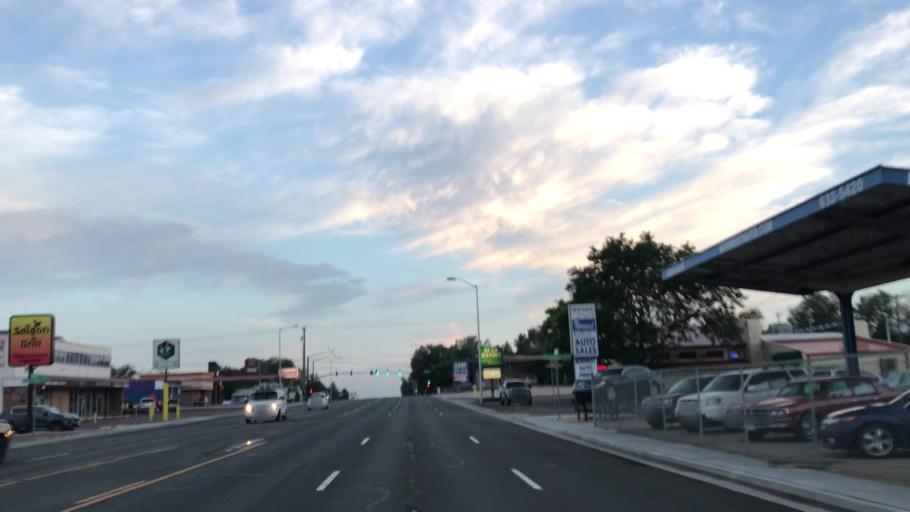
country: US
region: Colorado
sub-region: El Paso County
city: Colorado Springs
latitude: 38.8375
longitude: -104.7760
